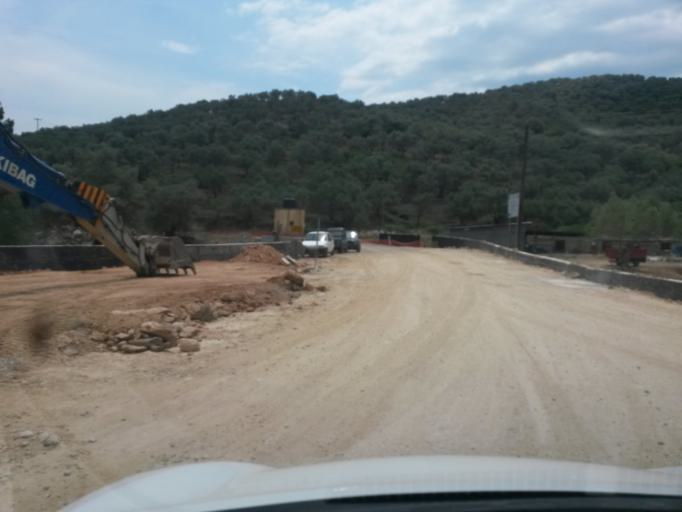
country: GR
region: North Aegean
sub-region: Nomos Lesvou
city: Pamfylla
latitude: 39.1787
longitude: 26.4221
